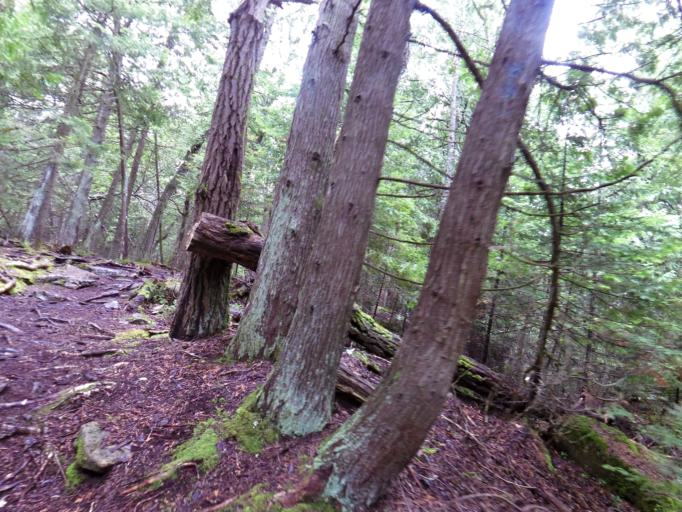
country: CA
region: Ontario
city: Tobermory
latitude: 45.2603
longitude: -81.6452
